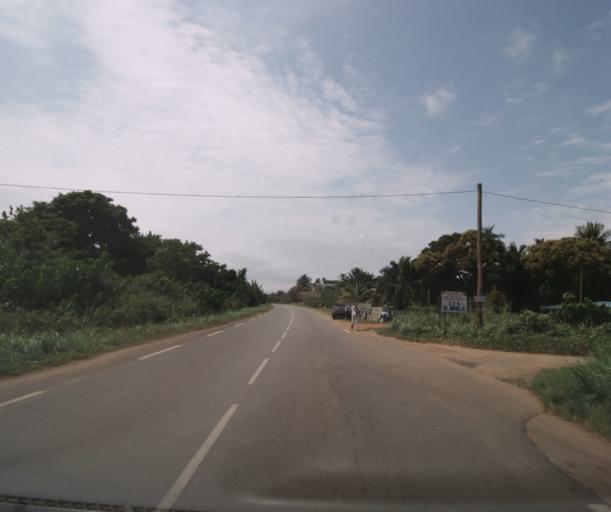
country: CM
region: South Province
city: Kribi
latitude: 3.0144
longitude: 9.9558
